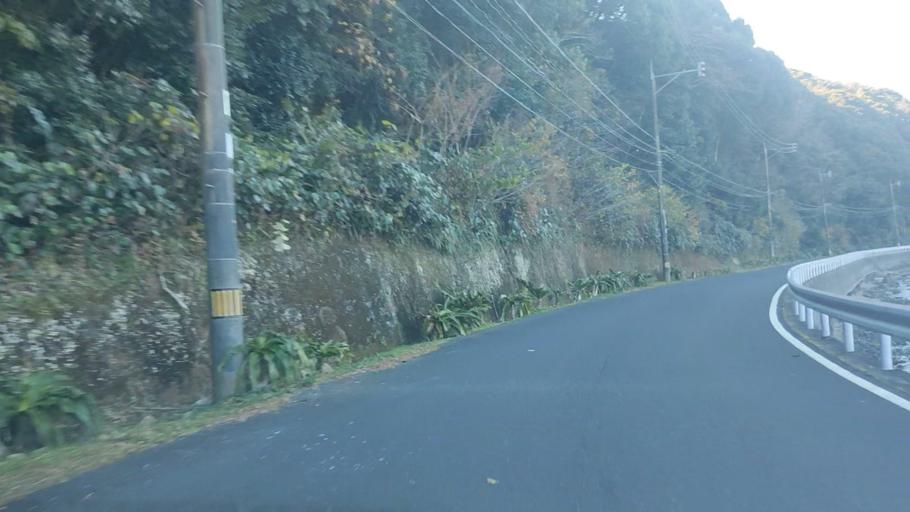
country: JP
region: Oita
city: Saiki
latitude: 32.8363
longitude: 131.9565
